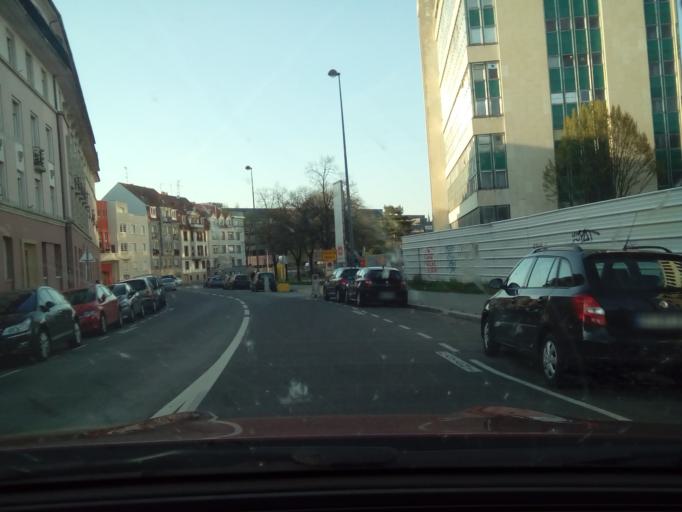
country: FR
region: Alsace
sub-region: Departement du Bas-Rhin
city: Strasbourg
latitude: 48.5760
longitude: 7.7384
